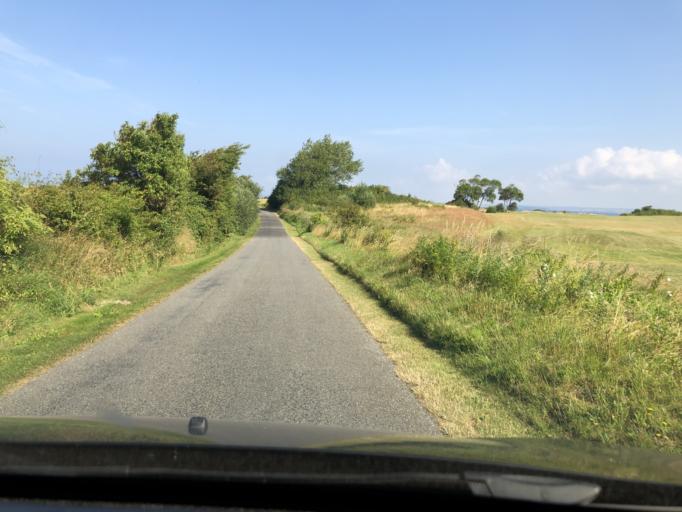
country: DK
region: South Denmark
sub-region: Faaborg-Midtfyn Kommune
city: Faaborg
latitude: 54.9652
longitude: 10.2114
